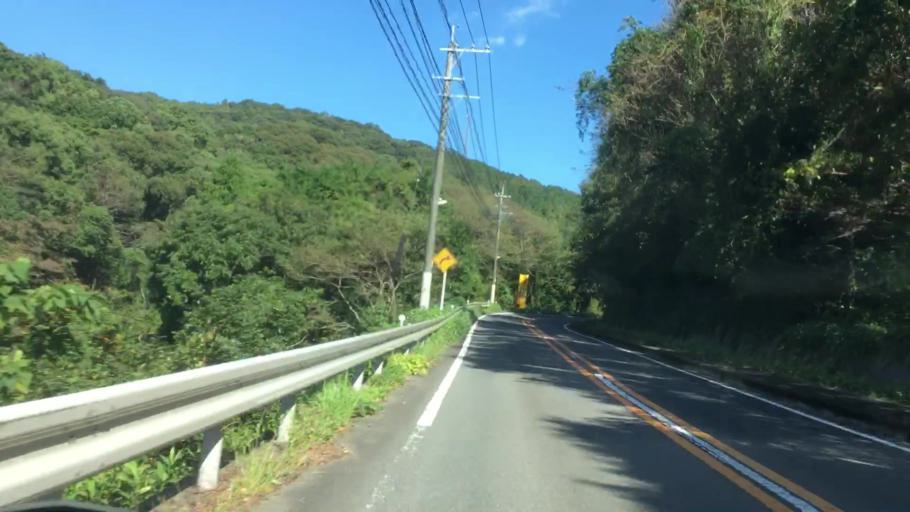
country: JP
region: Nagasaki
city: Sasebo
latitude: 33.0283
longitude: 129.6543
